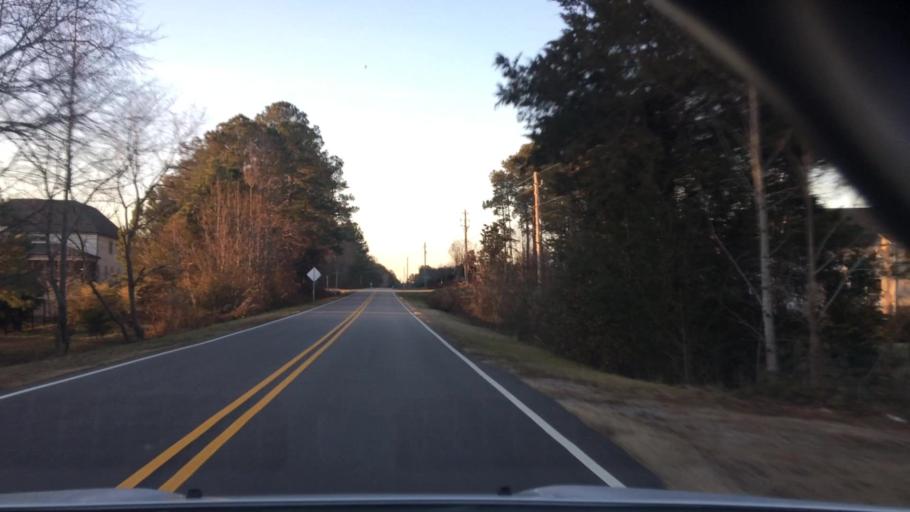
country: US
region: North Carolina
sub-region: Wake County
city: Rolesville
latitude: 35.9435
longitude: -78.4051
